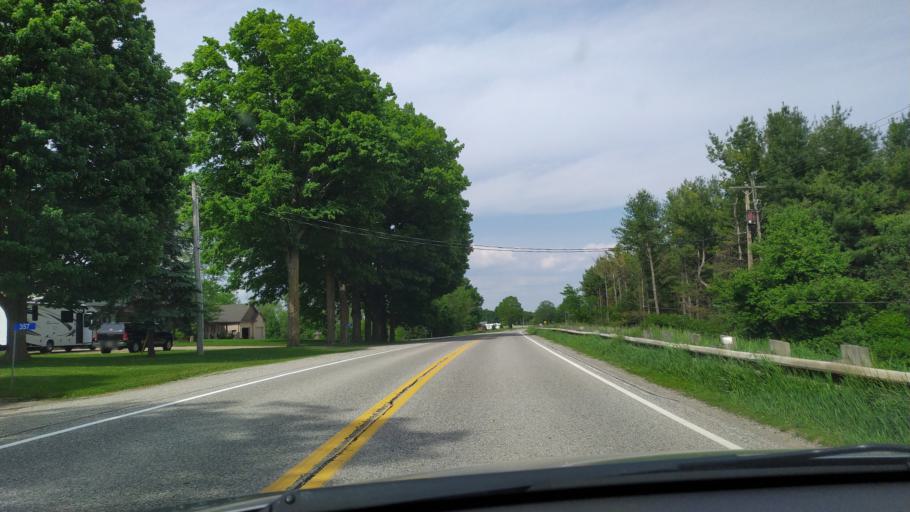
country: CA
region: Ontario
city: Dorchester
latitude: 43.0750
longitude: -81.0056
